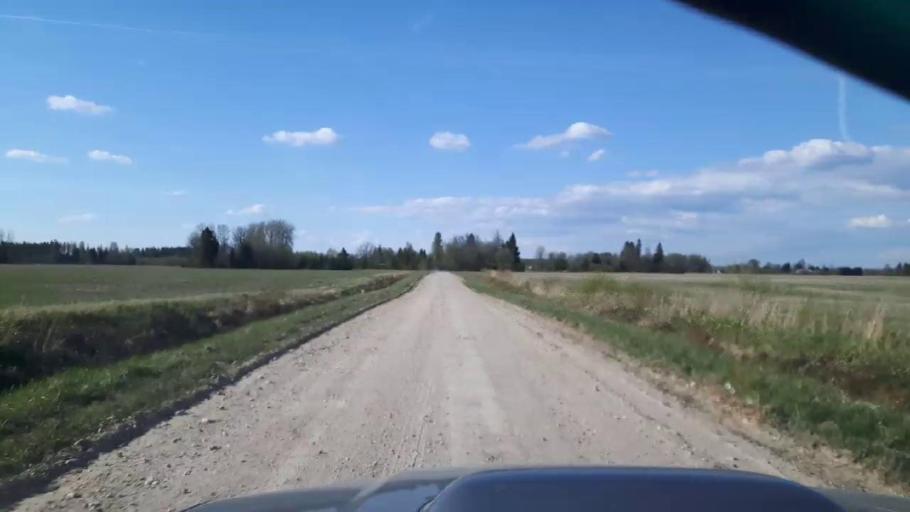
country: EE
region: Paernumaa
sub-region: Tootsi vald
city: Tootsi
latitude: 58.4404
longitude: 24.8550
